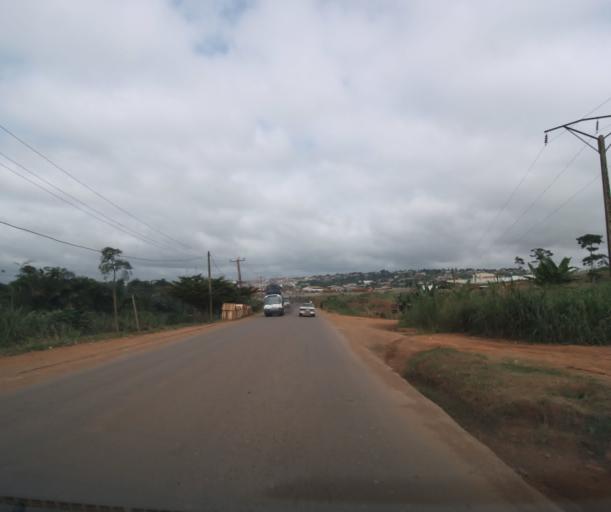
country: CM
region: Centre
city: Yaounde
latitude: 3.8072
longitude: 11.5170
